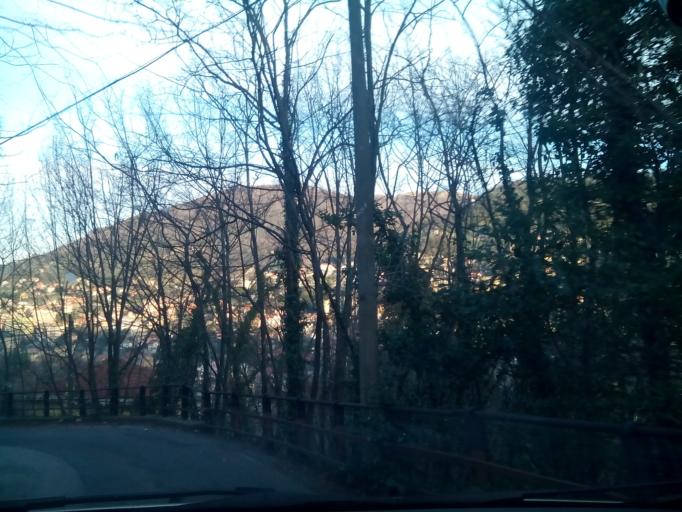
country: IT
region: Liguria
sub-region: Provincia di Genova
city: Piccarello
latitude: 44.4461
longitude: 9.0212
